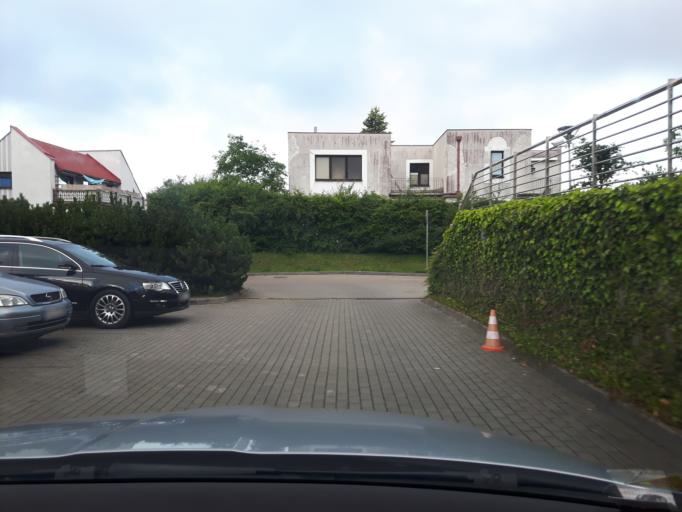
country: PL
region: Pomeranian Voivodeship
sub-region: Sopot
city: Sopot
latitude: 54.4779
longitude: 18.5541
